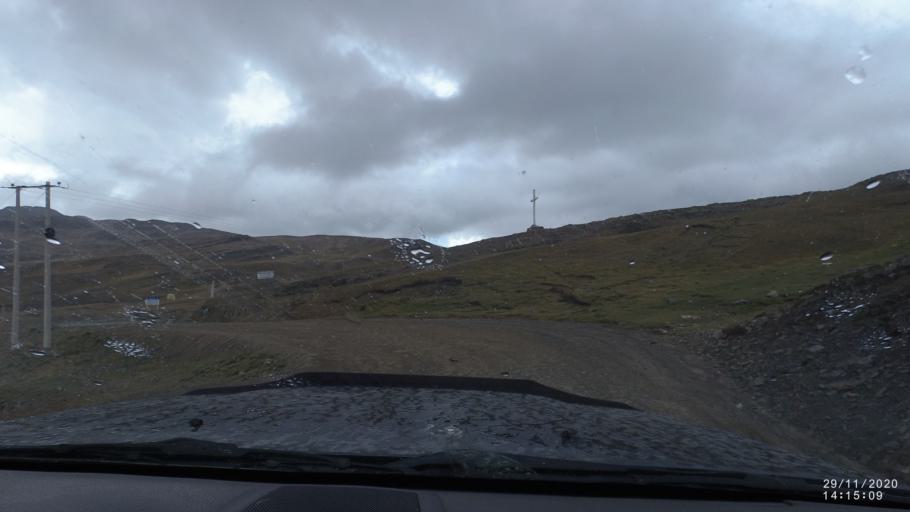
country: BO
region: Cochabamba
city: Sipe Sipe
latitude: -17.2476
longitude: -66.3934
